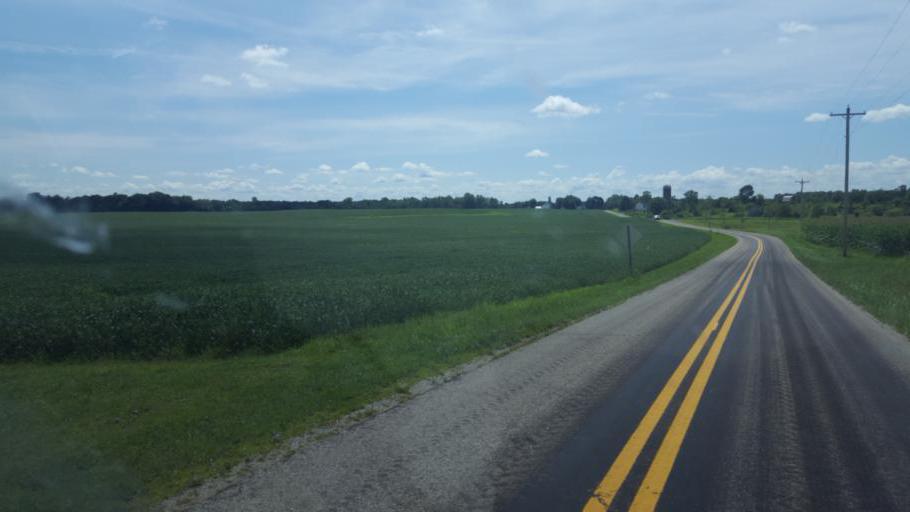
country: US
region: Ohio
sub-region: Delaware County
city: Sunbury
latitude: 40.3173
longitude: -82.8097
